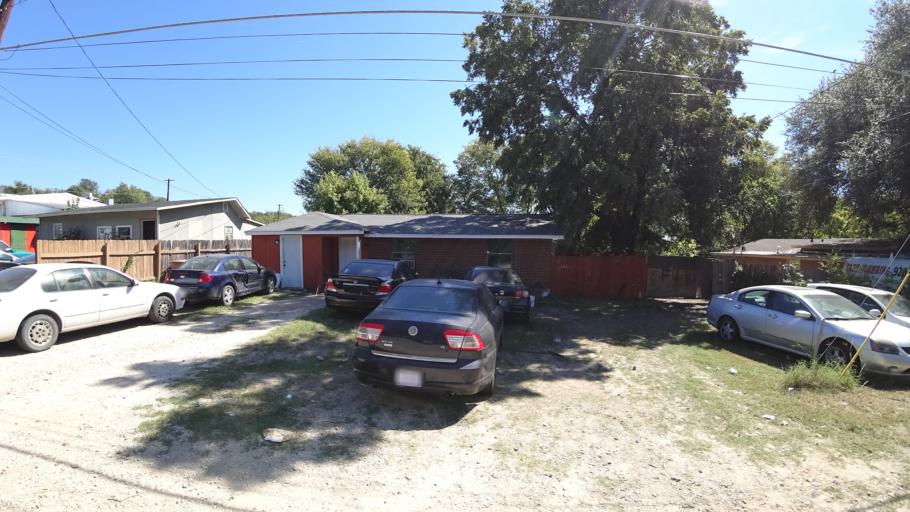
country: US
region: Texas
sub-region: Travis County
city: Hornsby Bend
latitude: 30.2793
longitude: -97.6458
